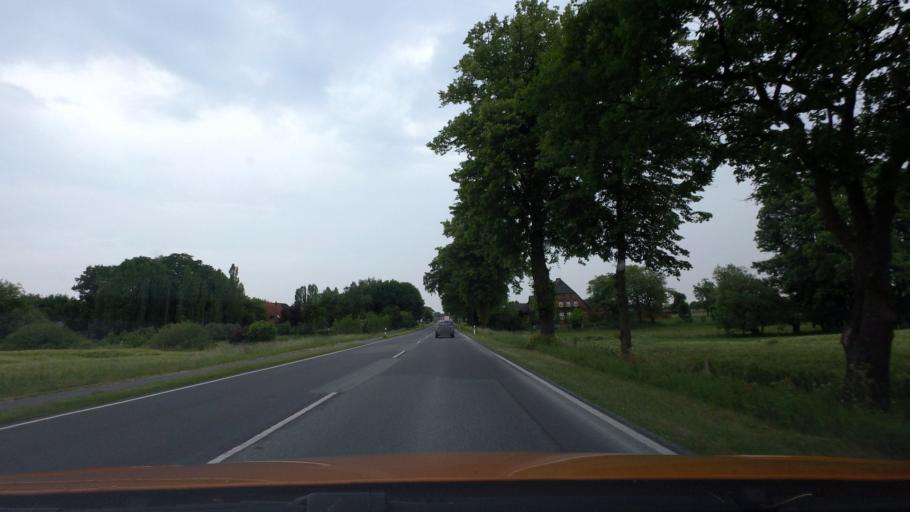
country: DE
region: Lower Saxony
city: Asendorf
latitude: 52.7637
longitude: 9.0123
